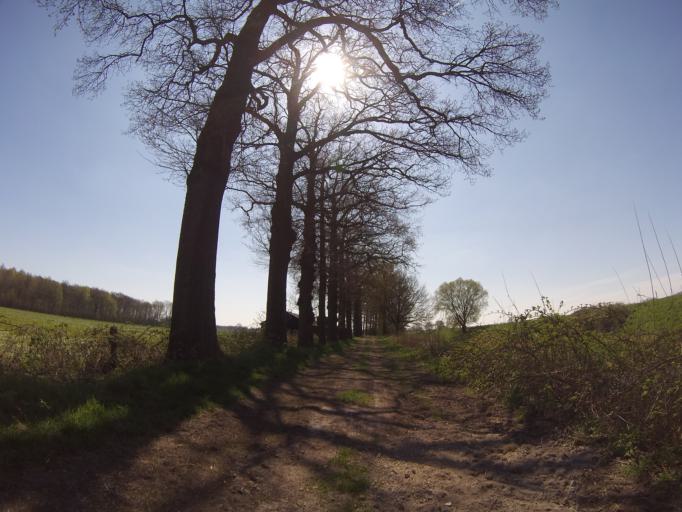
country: NL
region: Utrecht
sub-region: Gemeente Utrechtse Heuvelrug
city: Overberg
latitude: 52.0580
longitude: 5.4826
